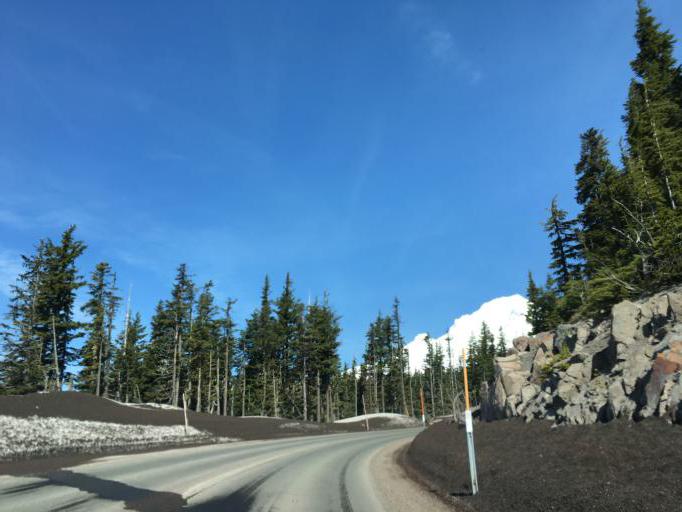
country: US
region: Oregon
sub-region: Clackamas County
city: Mount Hood Village
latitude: 45.3091
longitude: -121.7077
